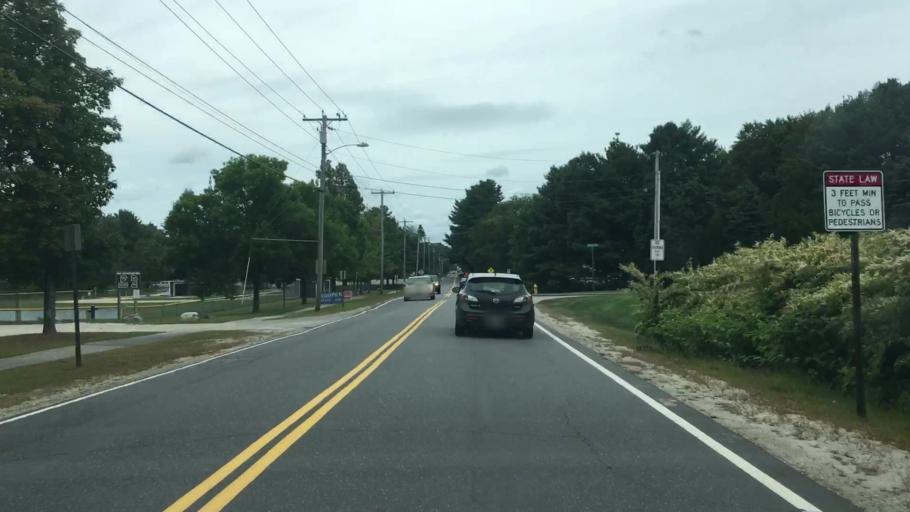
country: US
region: Maine
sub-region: Cumberland County
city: Yarmouth
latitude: 43.8096
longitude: -70.1764
